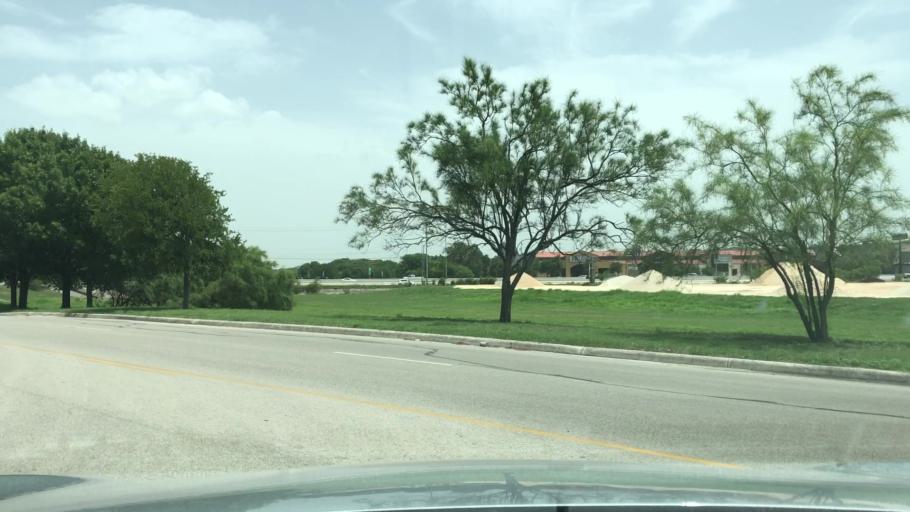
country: US
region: Texas
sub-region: Bexar County
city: Selma
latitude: 29.5819
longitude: -98.3155
